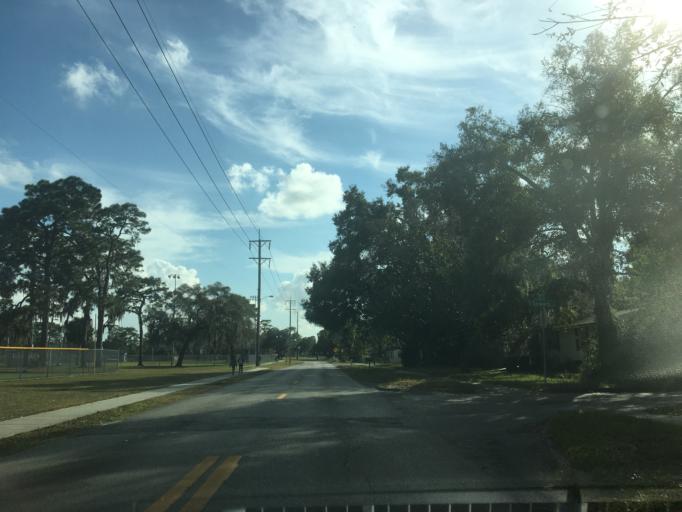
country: US
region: Florida
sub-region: Hillsborough County
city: University
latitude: 28.0284
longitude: -82.4347
